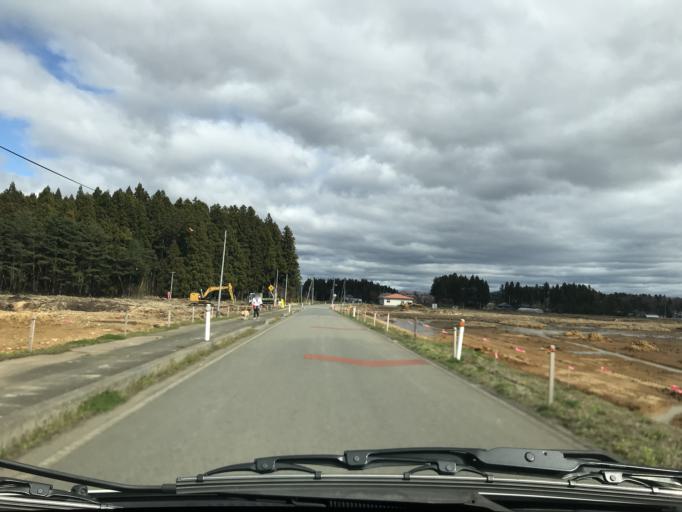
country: JP
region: Iwate
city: Mizusawa
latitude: 39.0997
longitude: 141.0524
